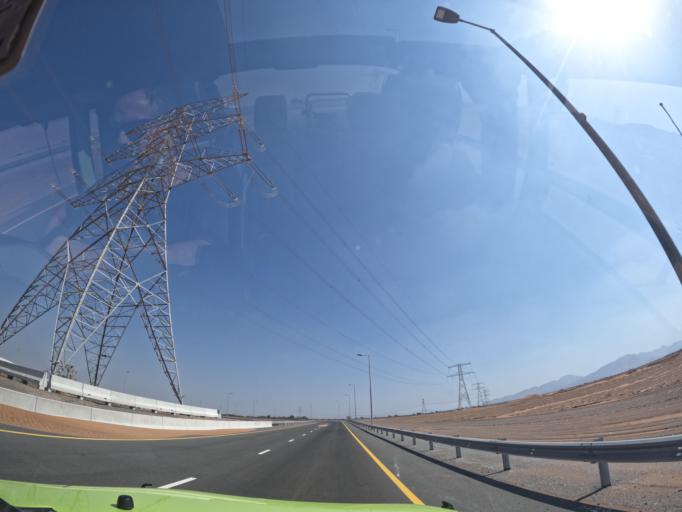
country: AE
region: Ash Shariqah
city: Adh Dhayd
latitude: 24.8121
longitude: 55.8031
